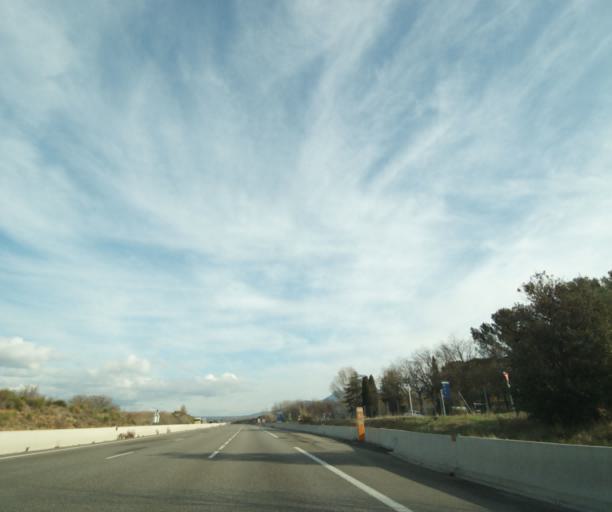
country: FR
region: Provence-Alpes-Cote d'Azur
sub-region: Departement des Bouches-du-Rhone
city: Peynier
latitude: 43.4699
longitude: 5.6556
